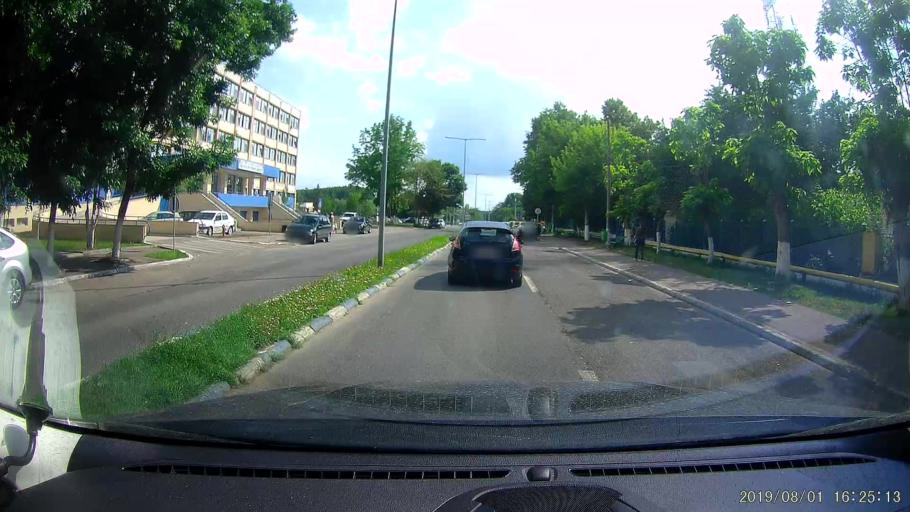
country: RO
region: Calarasi
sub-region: Municipiul Calarasi
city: Calarasi
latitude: 44.1928
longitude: 27.3268
